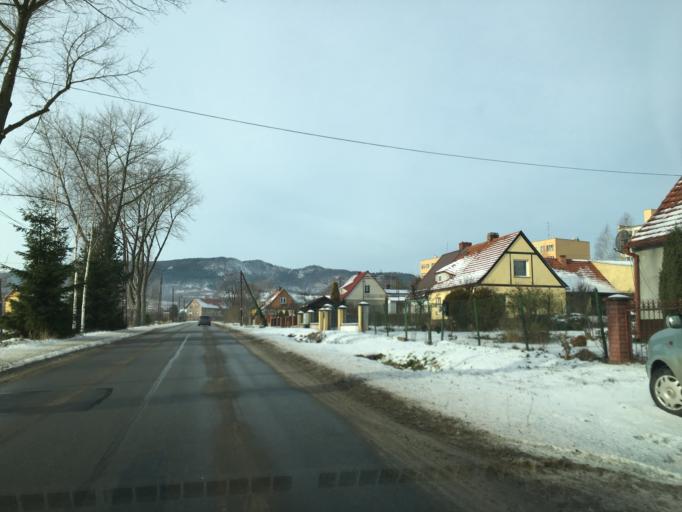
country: PL
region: Lower Silesian Voivodeship
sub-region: Powiat walbrzyski
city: Gluszyca
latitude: 50.6846
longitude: 16.3643
